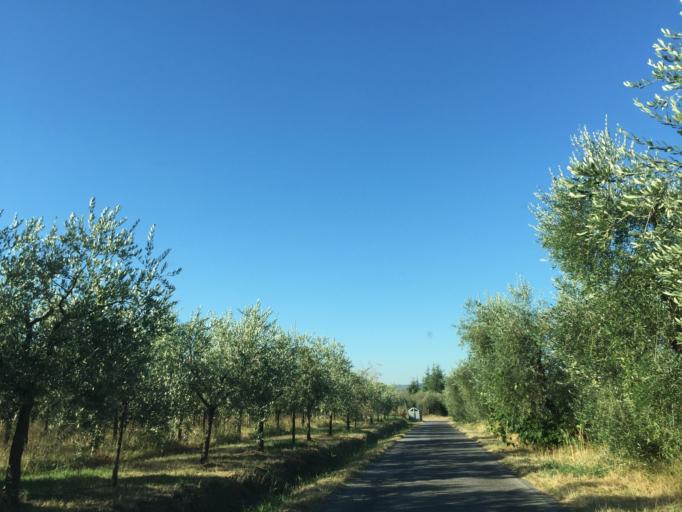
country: IT
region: Tuscany
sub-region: Provincia di Pistoia
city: Pistoia
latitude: 43.9463
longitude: 10.9406
